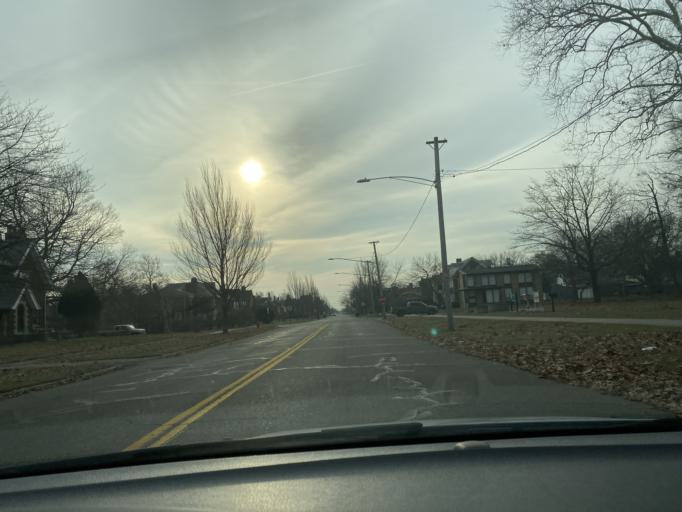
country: US
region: Michigan
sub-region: Wayne County
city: Highland Park
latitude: 42.3826
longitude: -83.1364
